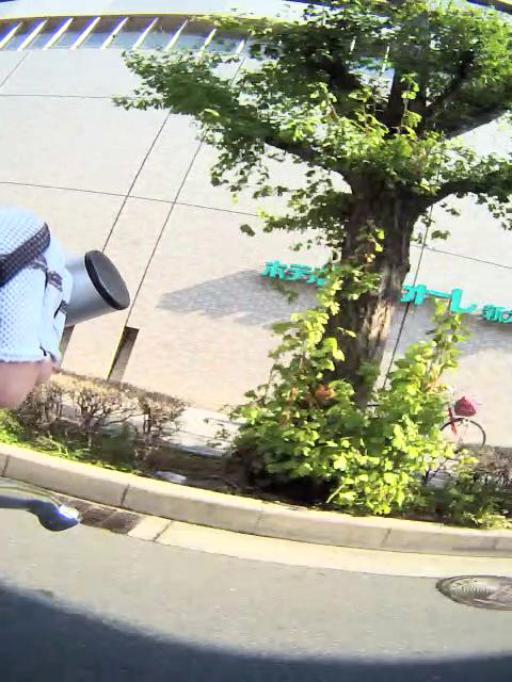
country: JP
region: Osaka
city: Suita
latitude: 34.7343
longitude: 135.4989
